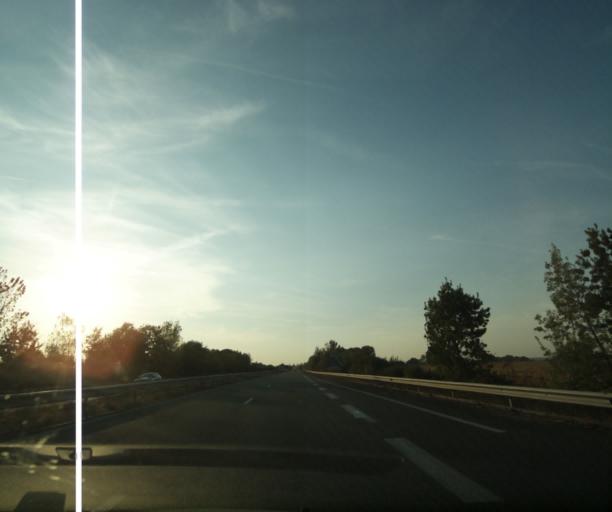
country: FR
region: Midi-Pyrenees
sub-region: Departement du Tarn-et-Garonne
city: Saint-Nicolas-de-la-Grave
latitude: 44.0455
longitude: 0.9932
